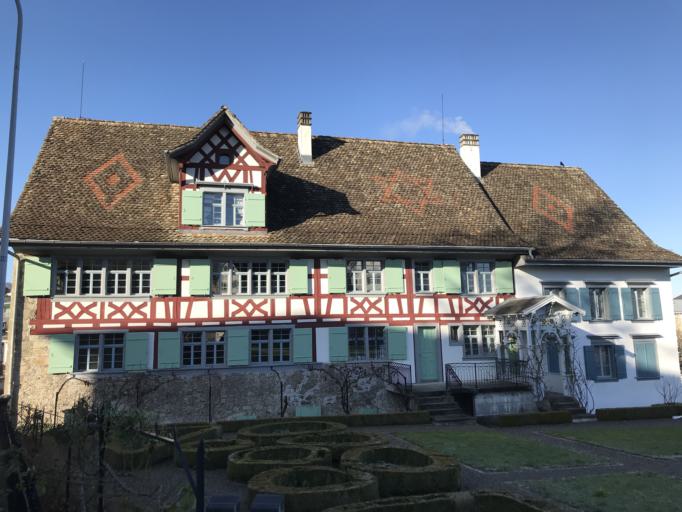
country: CH
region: Zurich
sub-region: Bezirk Horgen
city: Thalwil / Dorfkern
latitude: 47.2911
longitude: 8.5666
